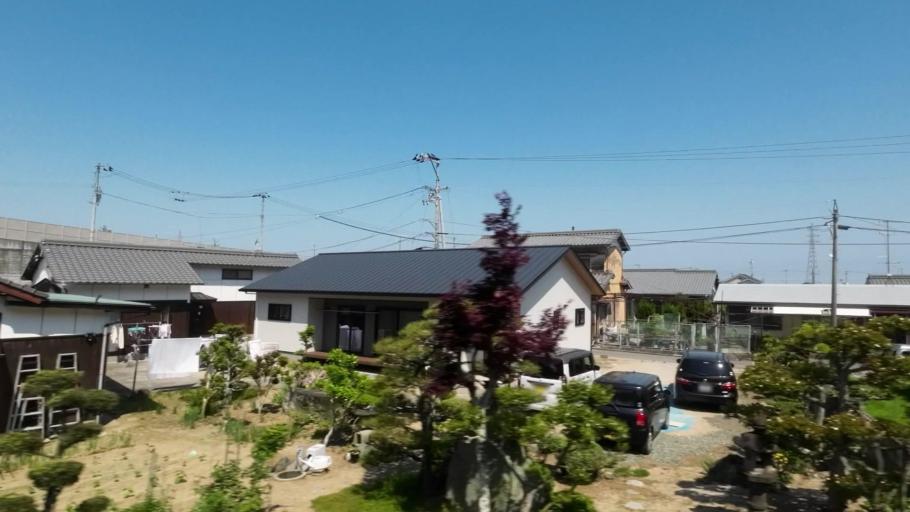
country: JP
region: Ehime
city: Niihama
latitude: 33.9580
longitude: 133.3058
